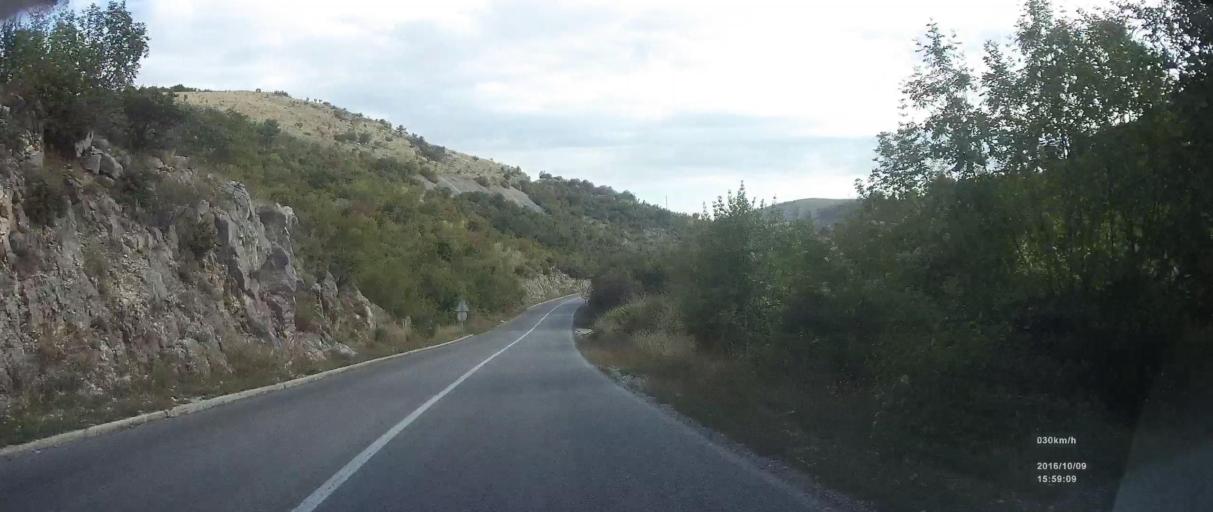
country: HR
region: Splitsko-Dalmatinska
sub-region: Grad Trogir
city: Trogir
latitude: 43.5705
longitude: 16.2460
